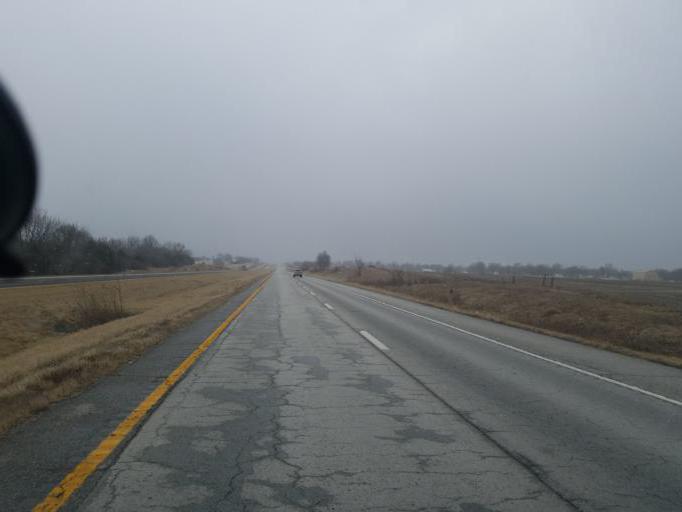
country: US
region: Missouri
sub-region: Macon County
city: La Plata
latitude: 39.9116
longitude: -92.4737
